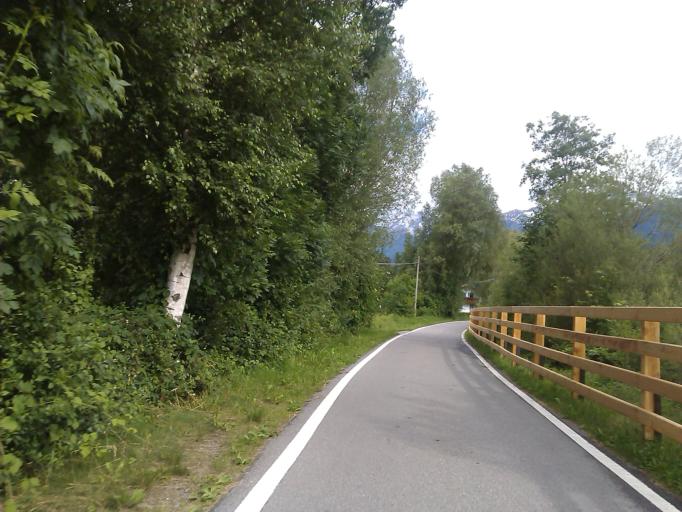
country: IT
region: Trentino-Alto Adige
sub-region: Bolzano
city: Glorenza
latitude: 46.6659
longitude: 10.5608
